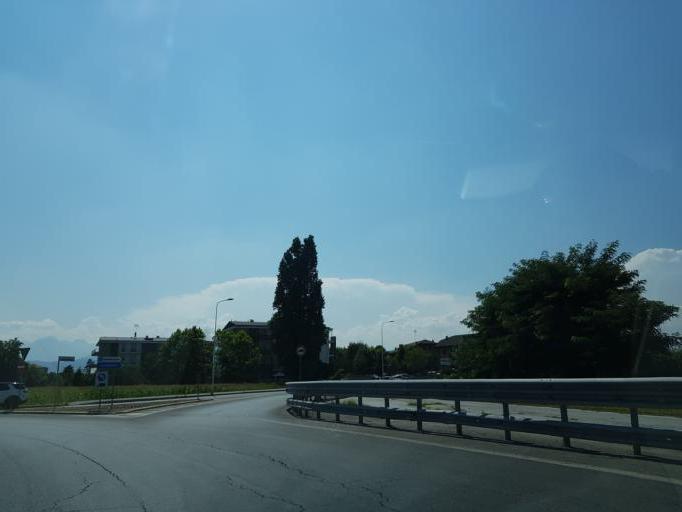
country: IT
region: Piedmont
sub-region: Provincia di Cuneo
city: Cuneo
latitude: 44.3938
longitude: 7.5246
